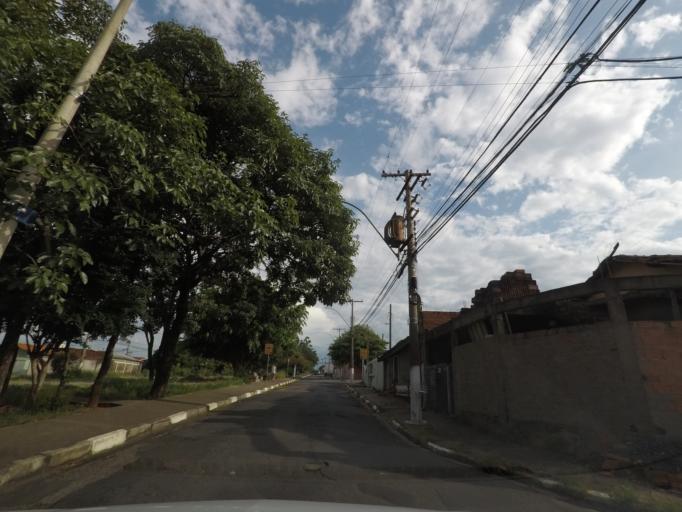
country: BR
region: Sao Paulo
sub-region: Campinas
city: Campinas
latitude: -22.9100
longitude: -47.1189
